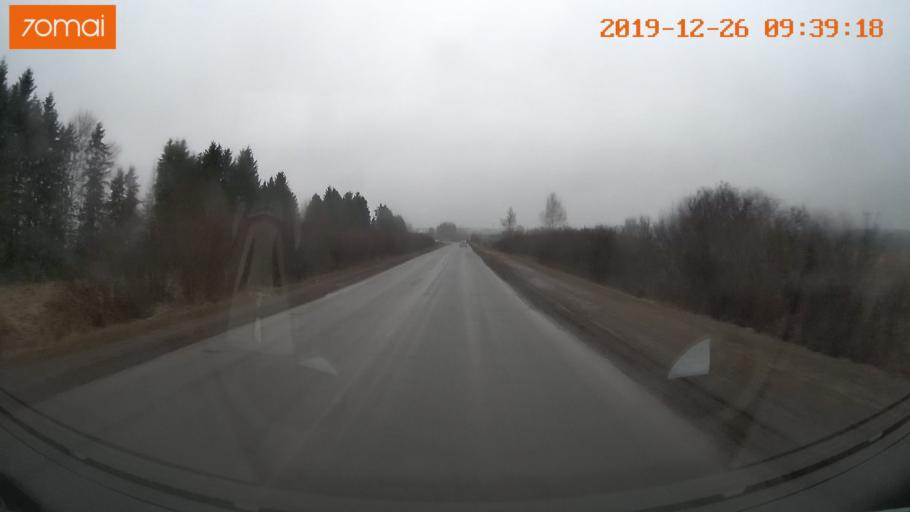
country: RU
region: Vologda
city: Vologda
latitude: 59.1530
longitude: 40.0278
